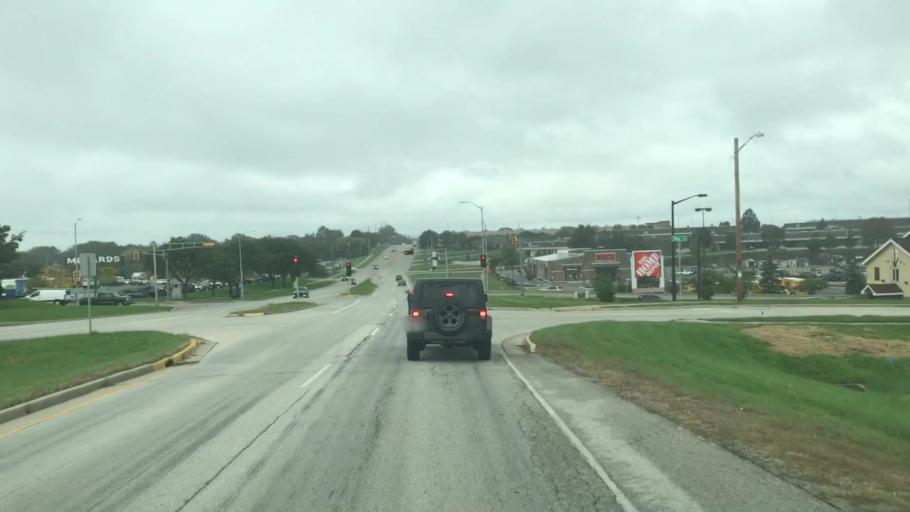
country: US
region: Wisconsin
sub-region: Waukesha County
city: Waukesha
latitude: 43.0365
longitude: -88.1779
